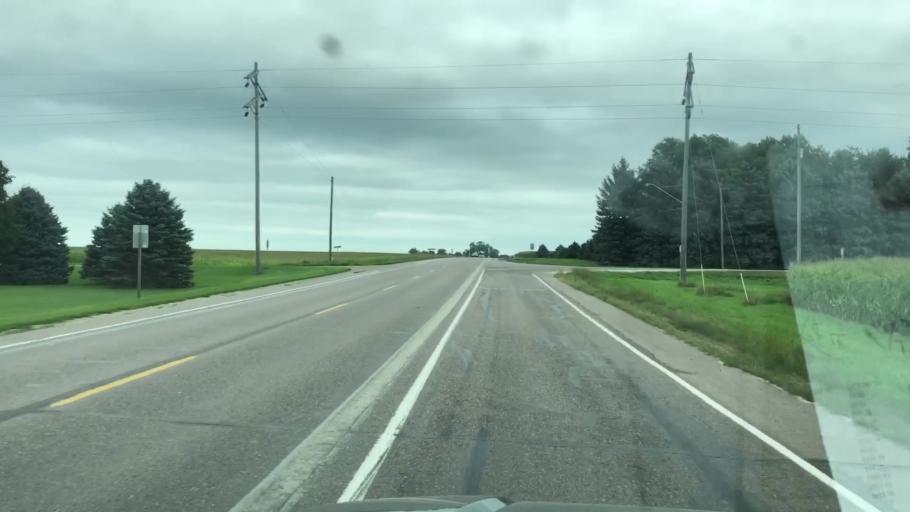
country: US
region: Iowa
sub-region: O'Brien County
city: Sheldon
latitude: 43.1862
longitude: -95.9811
